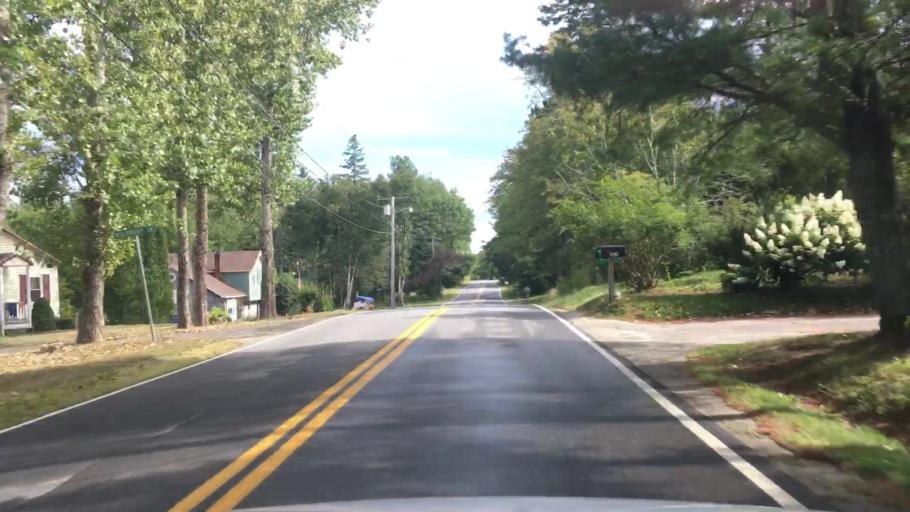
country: US
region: Maine
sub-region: Hancock County
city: Trenton
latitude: 44.4320
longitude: -68.3977
